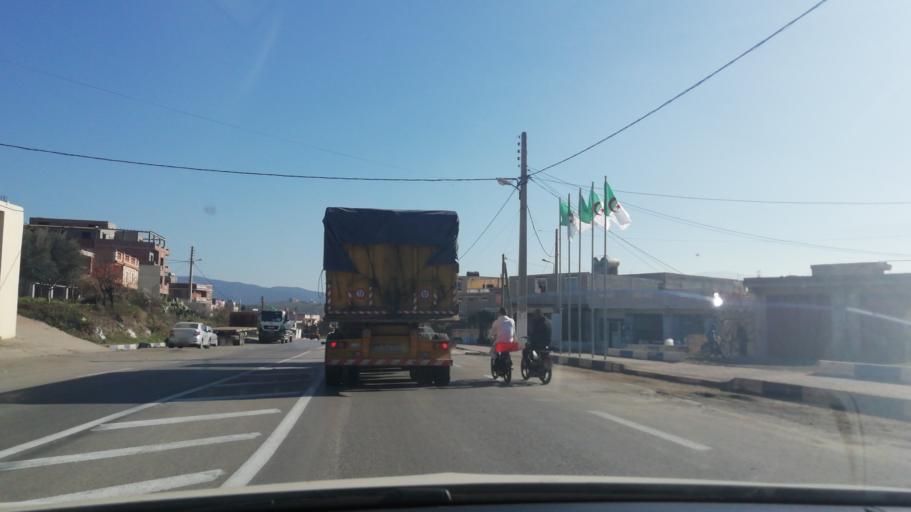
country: DZ
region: Tlemcen
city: Nedroma
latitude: 35.0765
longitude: -1.7851
